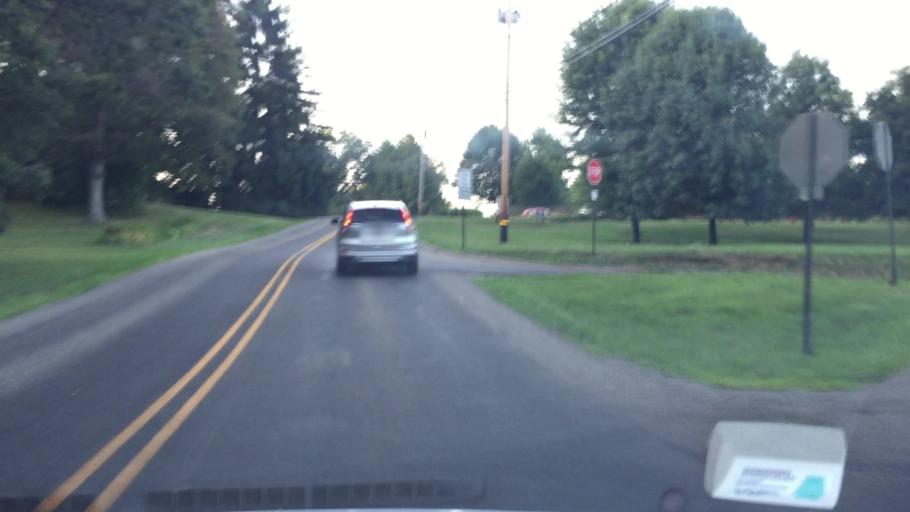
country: US
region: Pennsylvania
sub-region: Butler County
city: Seven Fields
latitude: 40.6961
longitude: -80.0502
